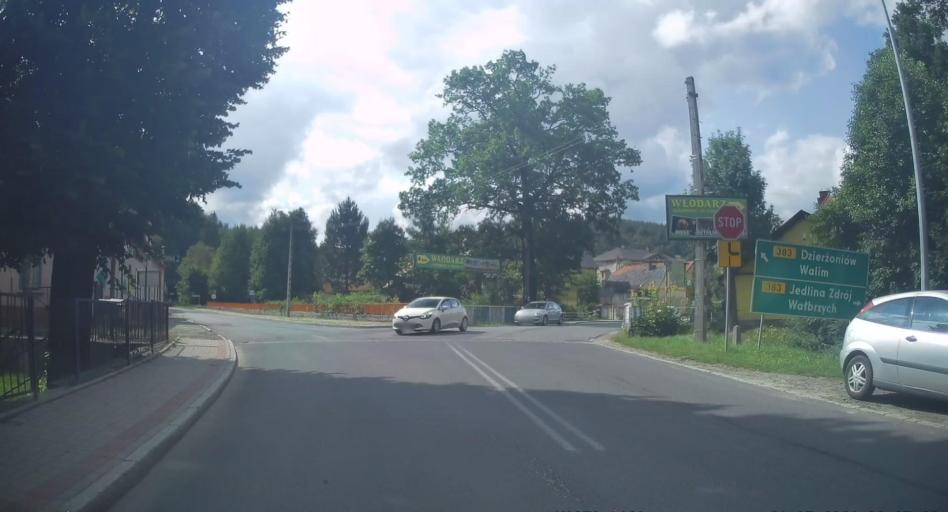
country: PL
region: Lower Silesian Voivodeship
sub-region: Powiat walbrzyski
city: Walim
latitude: 50.7311
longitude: 16.4033
